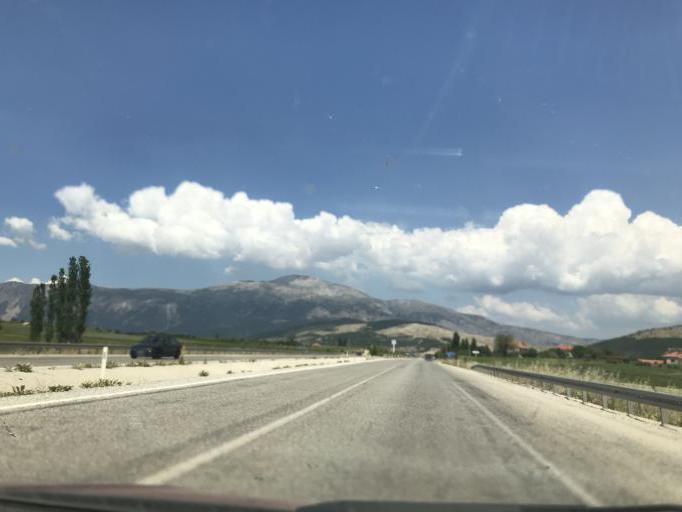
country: TR
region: Denizli
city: Serinhisar
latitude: 37.6191
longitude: 29.1896
